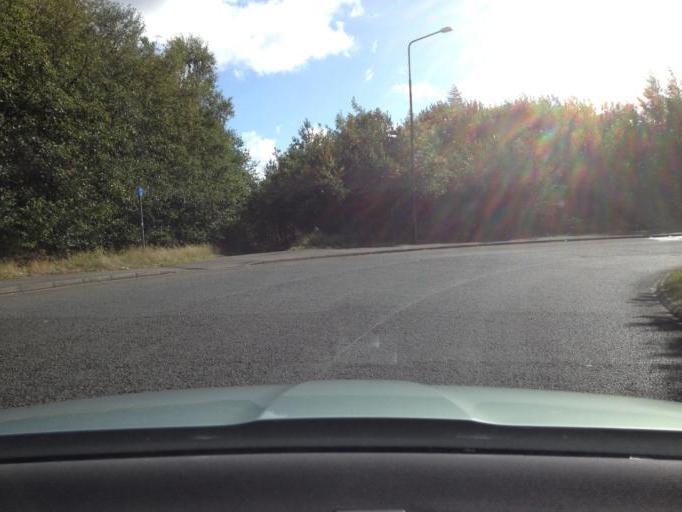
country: GB
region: Scotland
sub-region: West Lothian
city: West Calder
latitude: 55.8867
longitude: -3.5633
